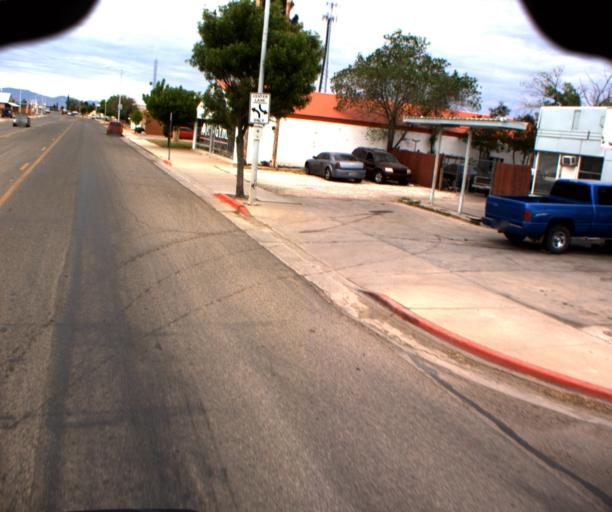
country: US
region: Arizona
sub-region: Cochise County
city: Willcox
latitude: 32.2514
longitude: -109.8333
